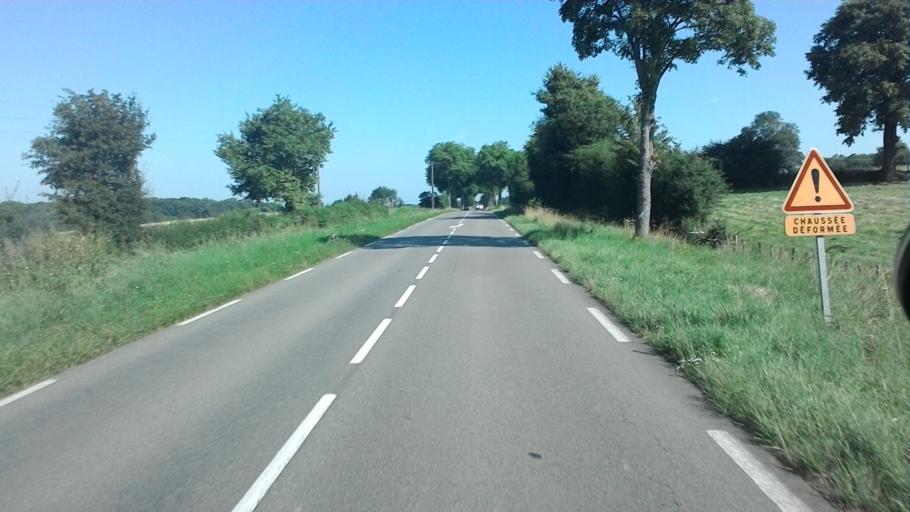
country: FR
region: Rhone-Alpes
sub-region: Departement de l'Ain
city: Saint-Trivier-de-Courtes
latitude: 46.4329
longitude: 5.0949
